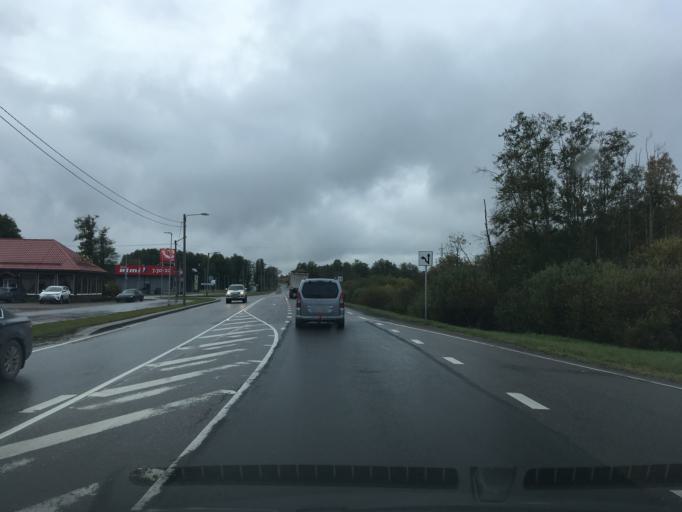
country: EE
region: Harju
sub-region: Saue vald
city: Laagri
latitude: 59.4066
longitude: 24.6176
